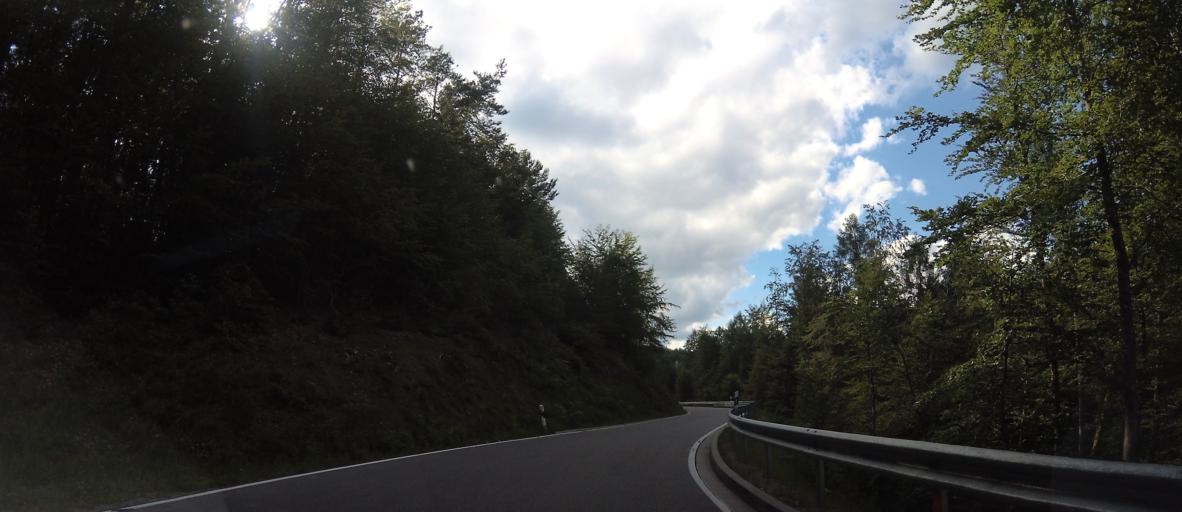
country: DE
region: Rheinland-Pfalz
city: Eppenbrunn
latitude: 49.1068
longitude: 7.6062
